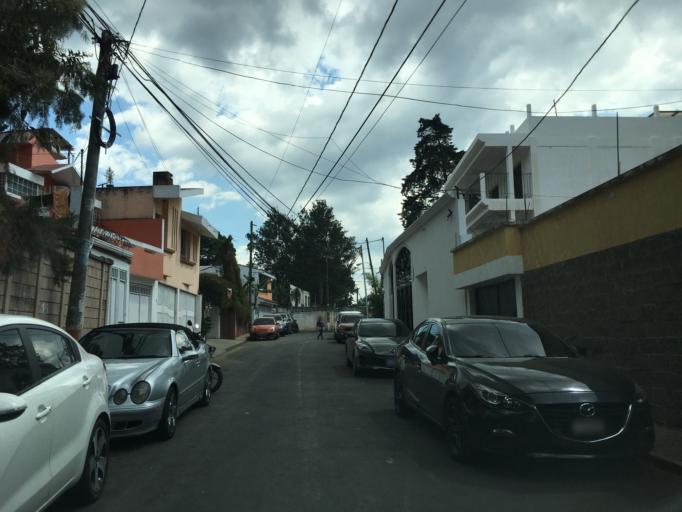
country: GT
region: Guatemala
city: Guatemala City
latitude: 14.6325
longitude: -90.4608
